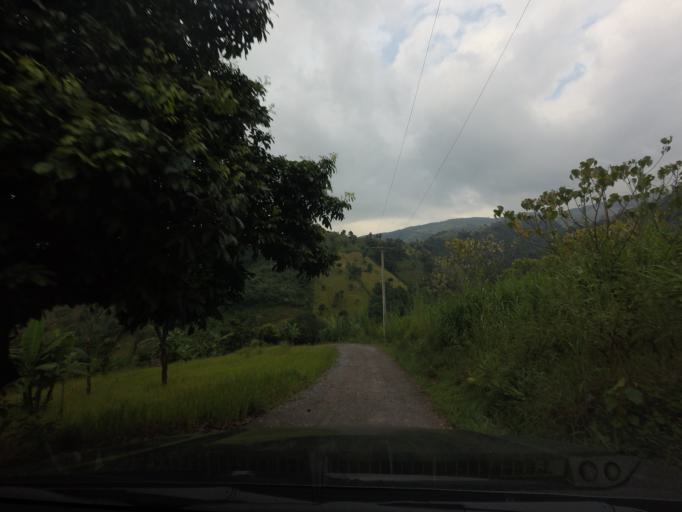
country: TH
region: Nan
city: Bo Kluea
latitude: 19.3510
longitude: 101.1779
